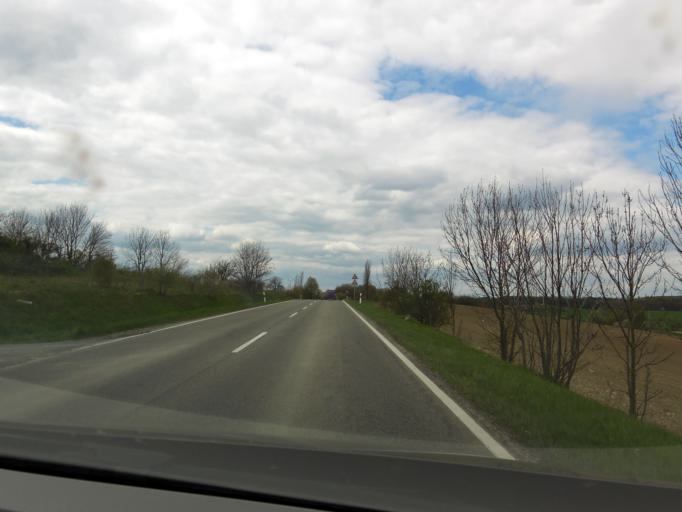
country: DE
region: Saxony-Anhalt
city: Eckartsberga
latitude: 51.1204
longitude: 11.5735
